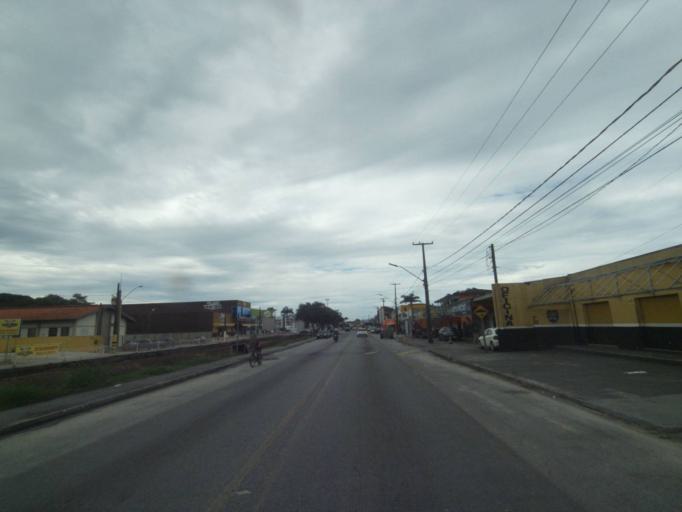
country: BR
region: Parana
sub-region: Guaratuba
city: Guaratuba
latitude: -25.8233
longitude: -48.5408
